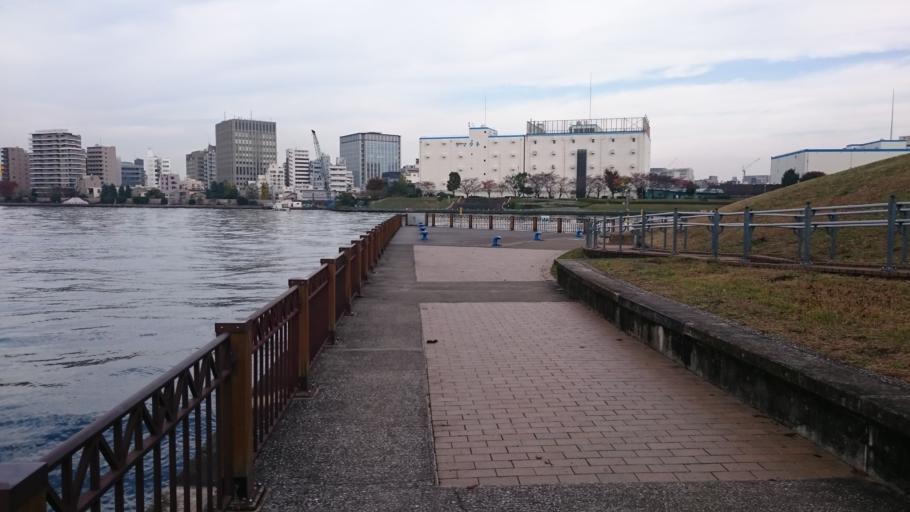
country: JP
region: Tokyo
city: Tokyo
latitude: 35.6713
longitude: 139.7857
